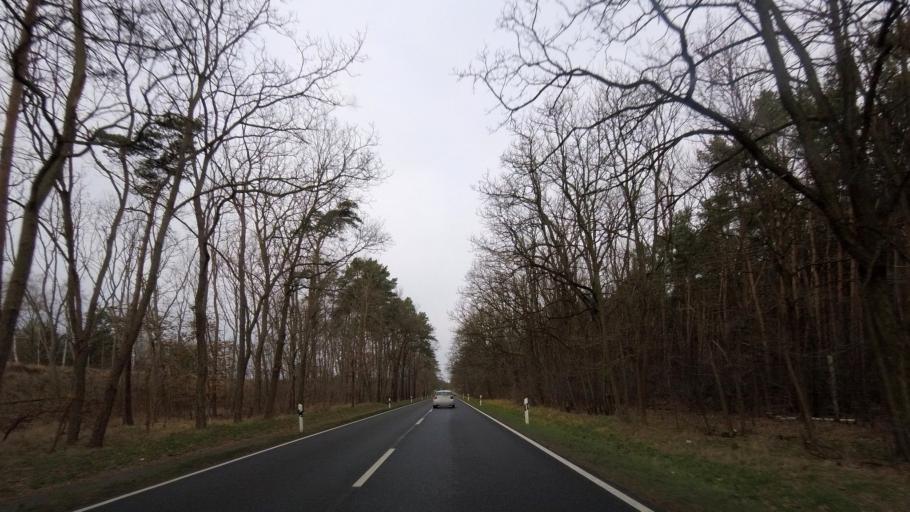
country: DE
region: Brandenburg
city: Treuenbrietzen
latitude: 52.0623
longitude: 12.8978
